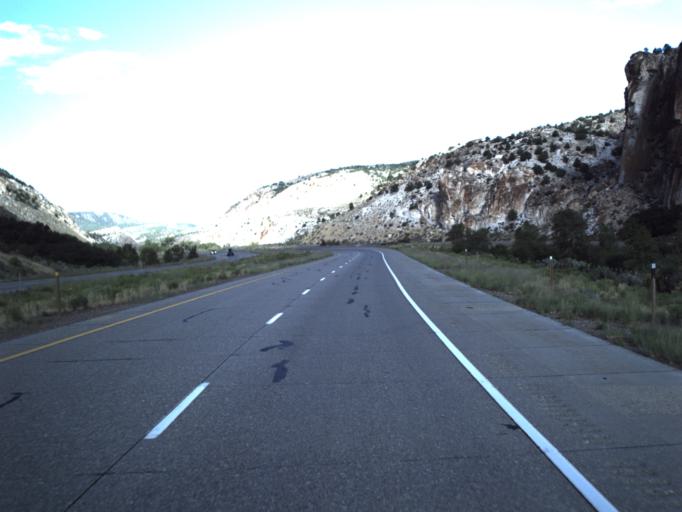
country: US
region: Utah
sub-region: Sevier County
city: Monroe
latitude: 38.5794
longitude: -112.2904
